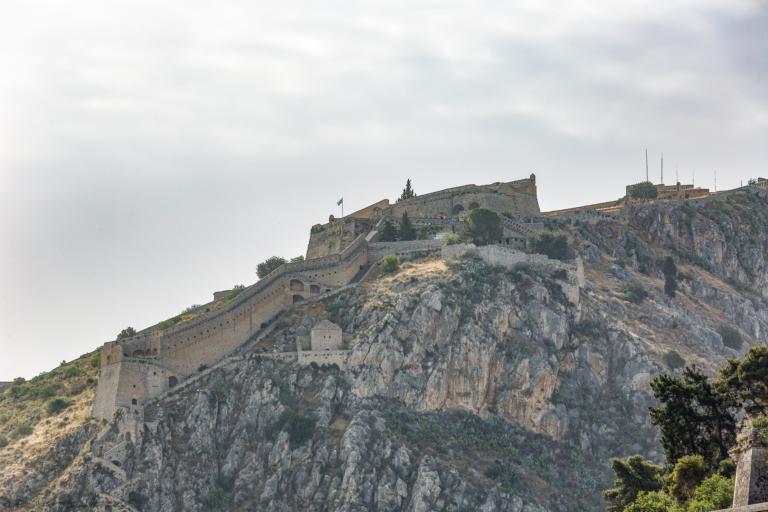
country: GR
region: Peloponnese
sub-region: Nomos Argolidos
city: Nafplio
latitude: 37.5676
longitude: 22.7959
